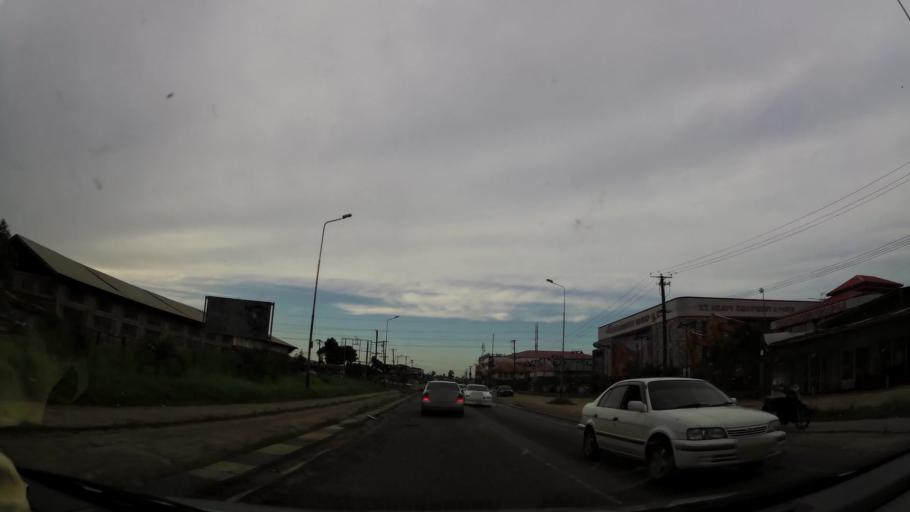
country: SR
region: Paramaribo
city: Paramaribo
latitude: 5.8033
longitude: -55.1884
